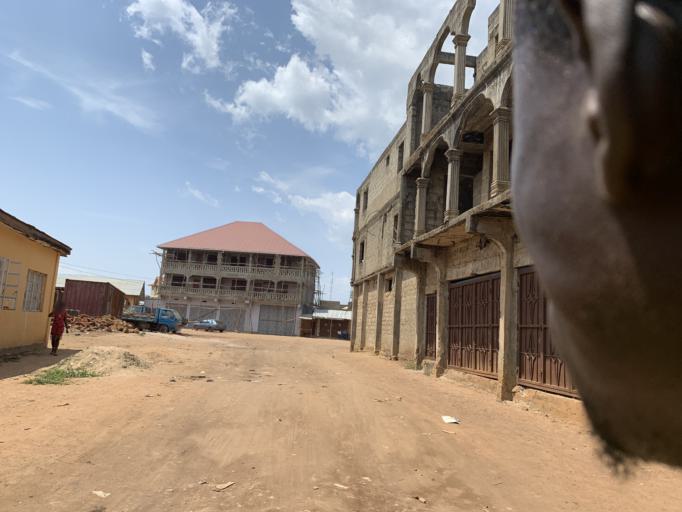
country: SL
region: Western Area
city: Waterloo
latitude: 8.3355
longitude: -13.0418
